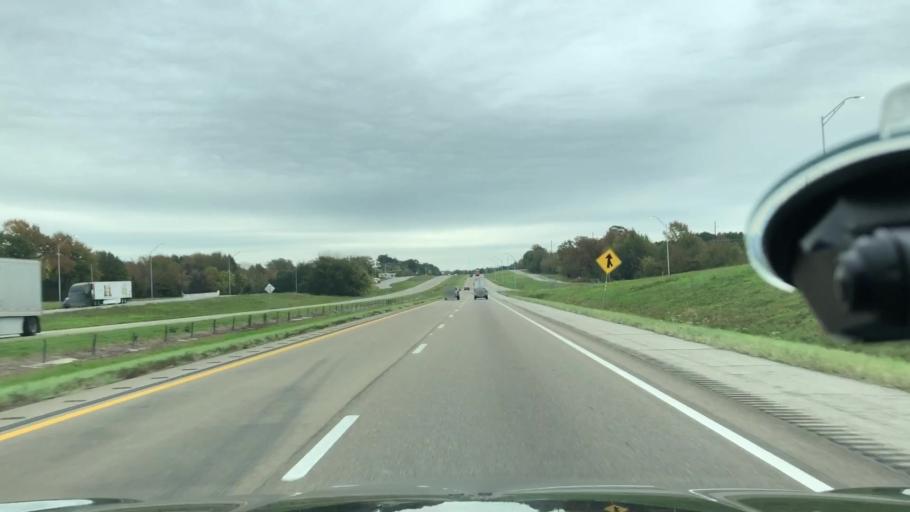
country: US
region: Texas
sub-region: Titus County
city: Mount Pleasant
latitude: 33.1586
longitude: -95.0503
